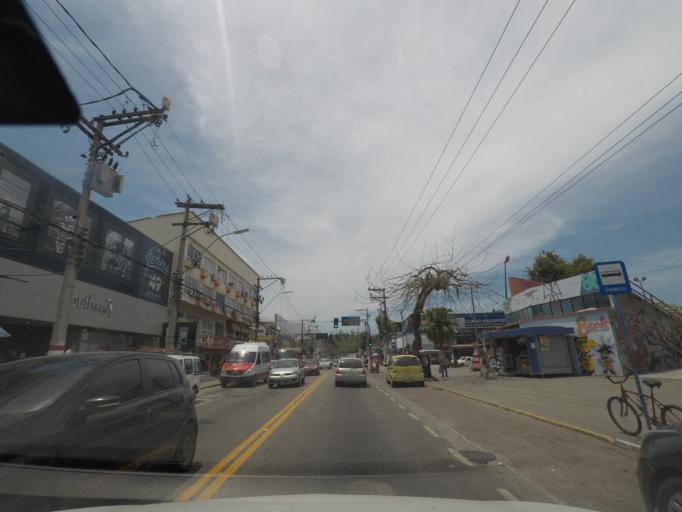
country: BR
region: Rio de Janeiro
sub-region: Marica
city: Marica
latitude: -22.9194
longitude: -42.8182
